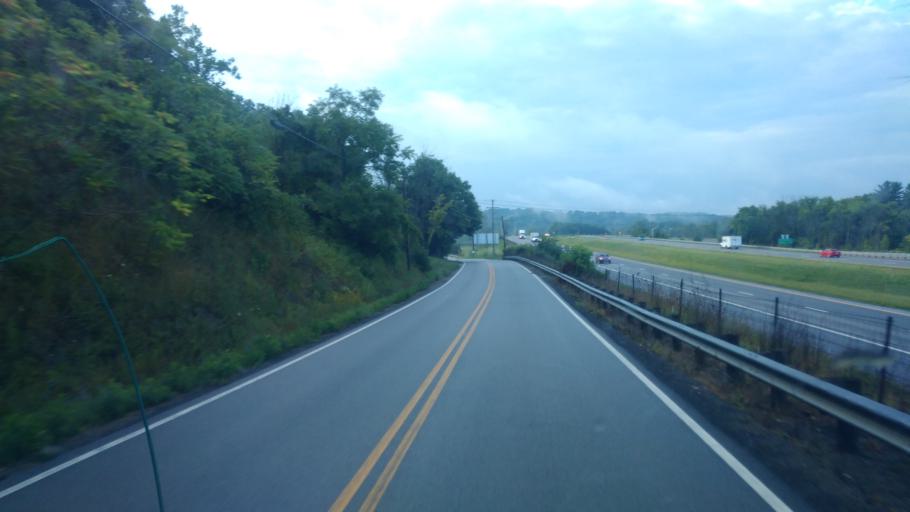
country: US
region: Ohio
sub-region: Guernsey County
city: Byesville
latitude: 39.9730
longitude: -81.5343
